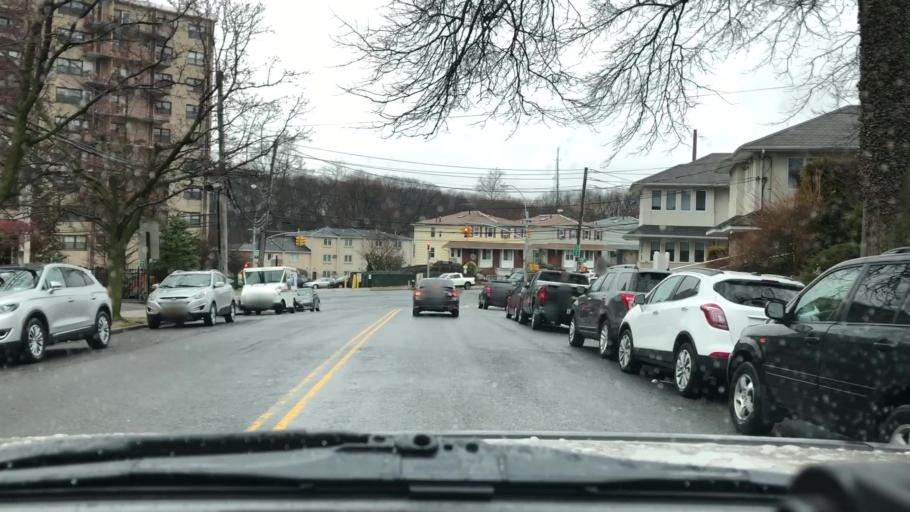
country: US
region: New Jersey
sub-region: Hudson County
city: Bayonne
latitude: 40.6210
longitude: -74.1092
